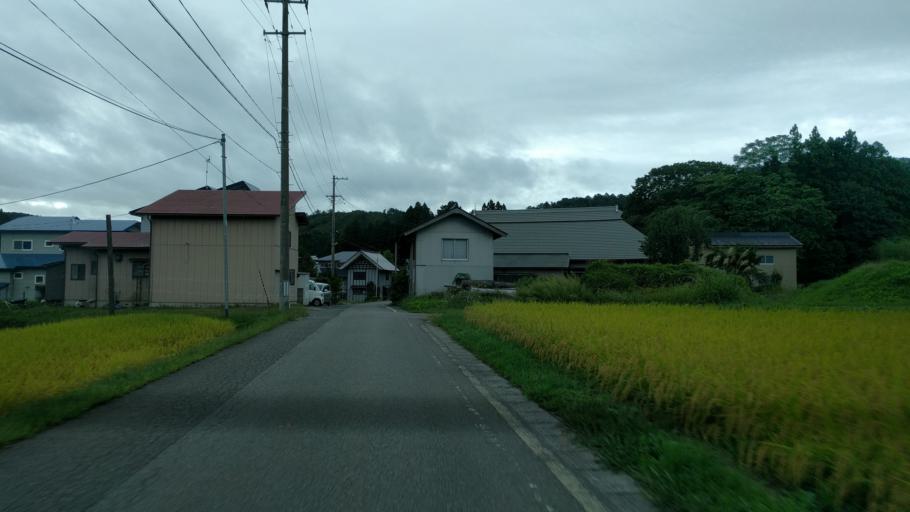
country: JP
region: Fukushima
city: Kitakata
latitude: 37.5438
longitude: 139.7300
